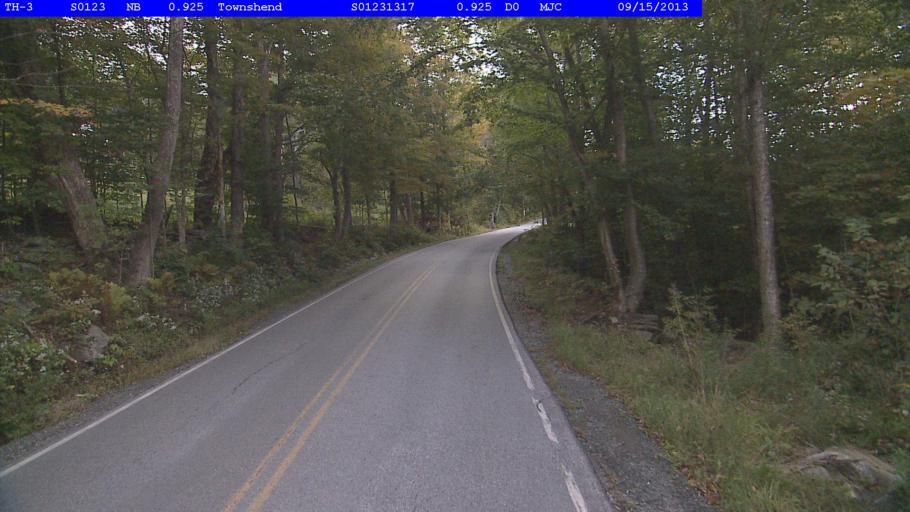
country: US
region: Vermont
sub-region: Windham County
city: Newfane
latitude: 43.0962
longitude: -72.7097
